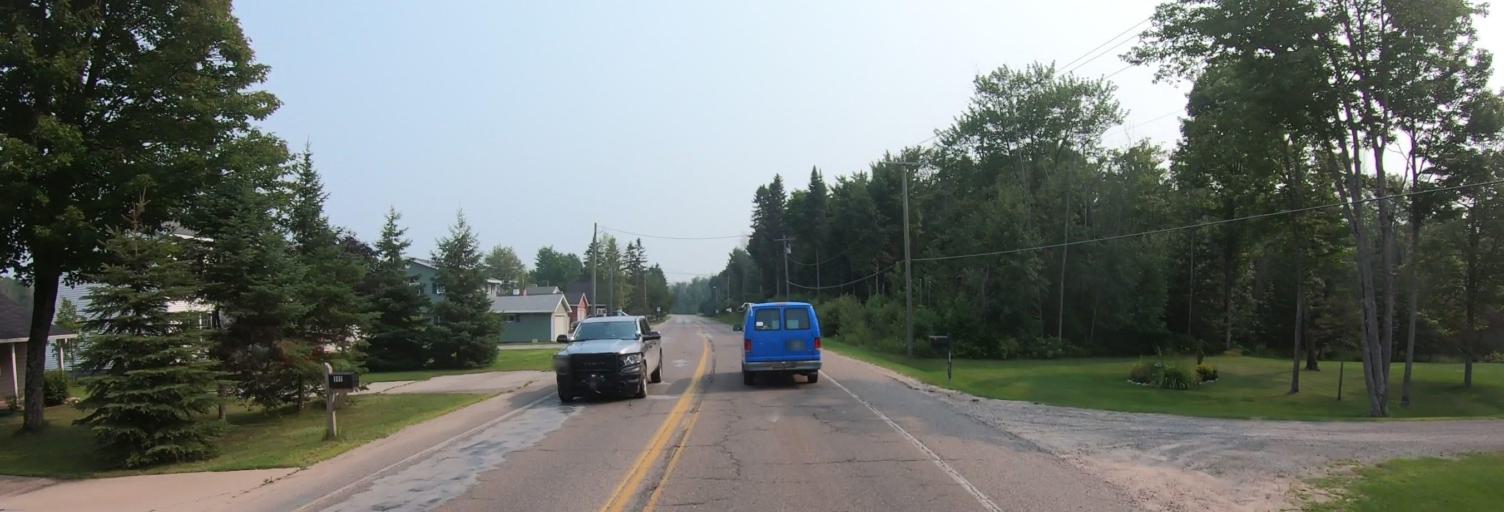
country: US
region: Michigan
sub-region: Chippewa County
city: Sault Ste. Marie
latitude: 46.4769
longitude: -84.3042
